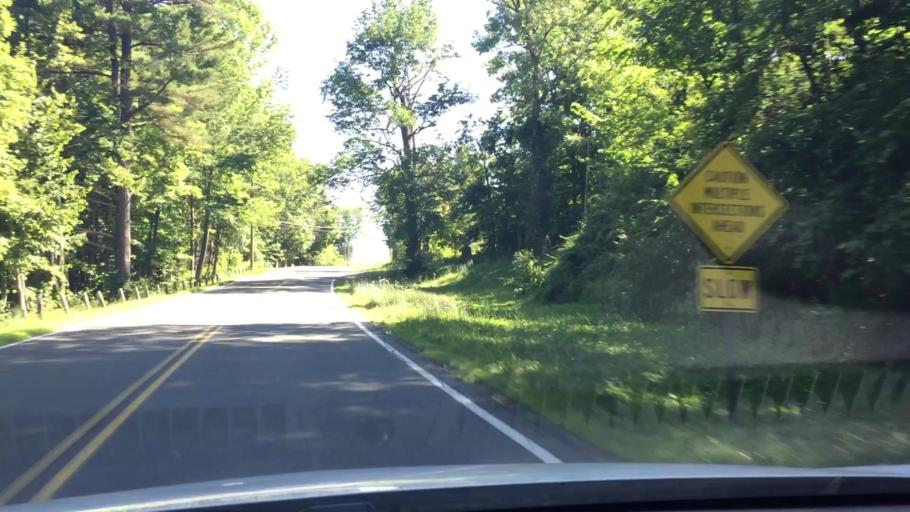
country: US
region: Massachusetts
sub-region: Berkshire County
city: Richmond
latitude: 42.3979
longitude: -73.3330
